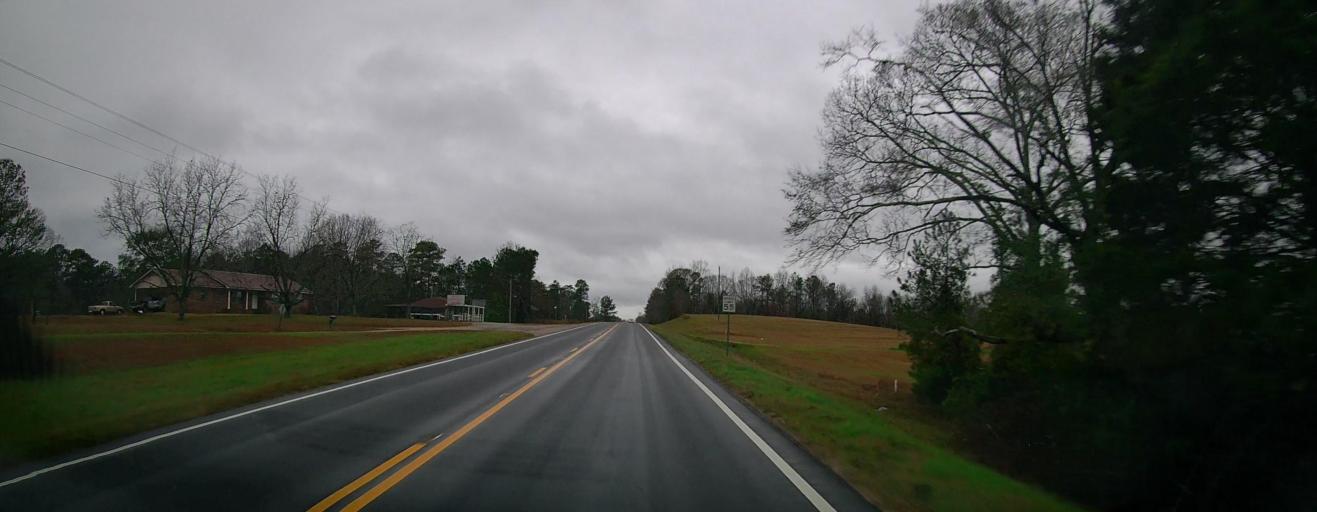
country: US
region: Alabama
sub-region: Chilton County
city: Thorsby
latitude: 32.8003
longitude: -86.9127
